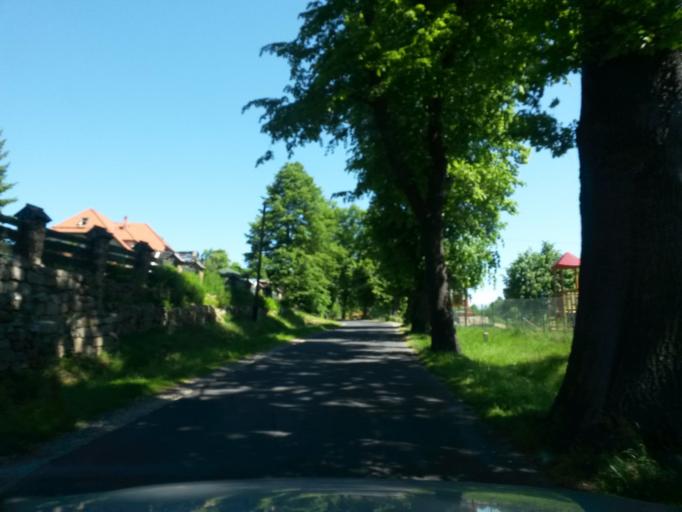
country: PL
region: Lower Silesian Voivodeship
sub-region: Powiat jeleniogorski
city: Podgorzyn
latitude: 50.8250
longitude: 15.6607
